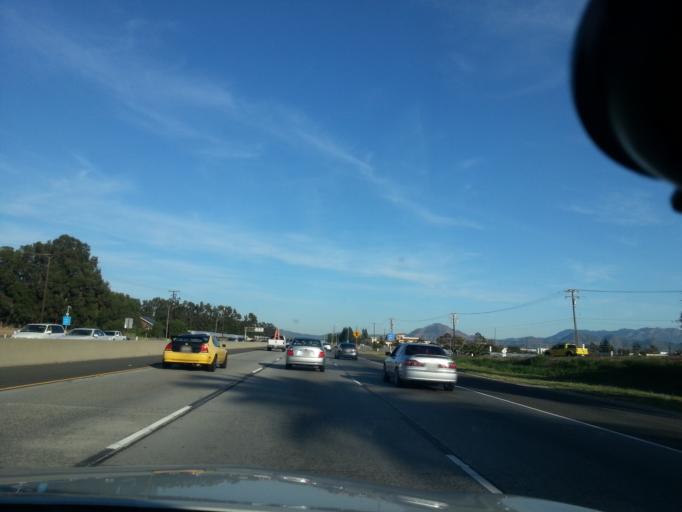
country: US
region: California
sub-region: Ventura County
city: El Rio
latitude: 34.2216
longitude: -119.1015
